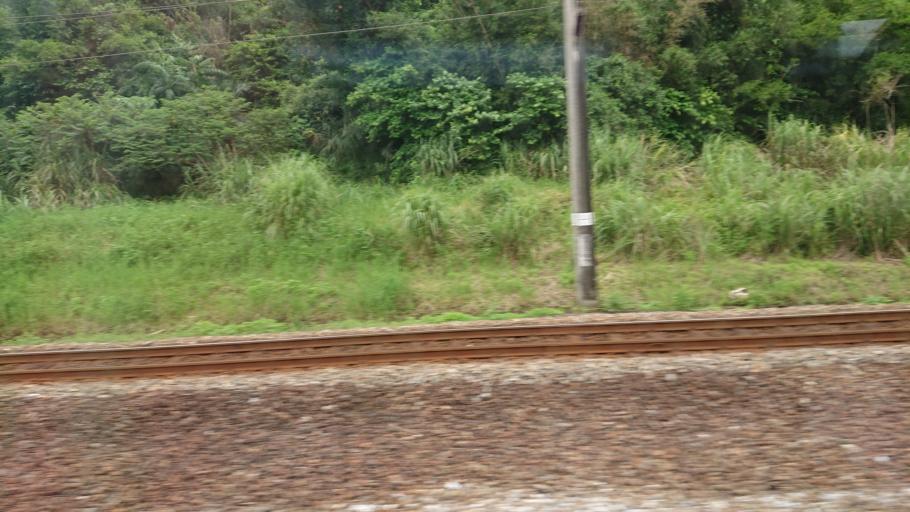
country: TW
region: Taiwan
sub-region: Yilan
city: Yilan
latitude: 24.9058
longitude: 121.8701
